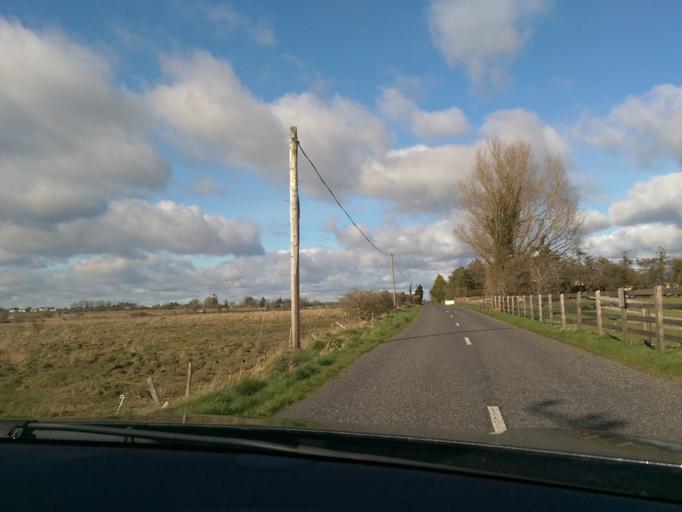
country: IE
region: Connaught
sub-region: County Galway
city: Athenry
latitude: 53.4335
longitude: -8.5693
